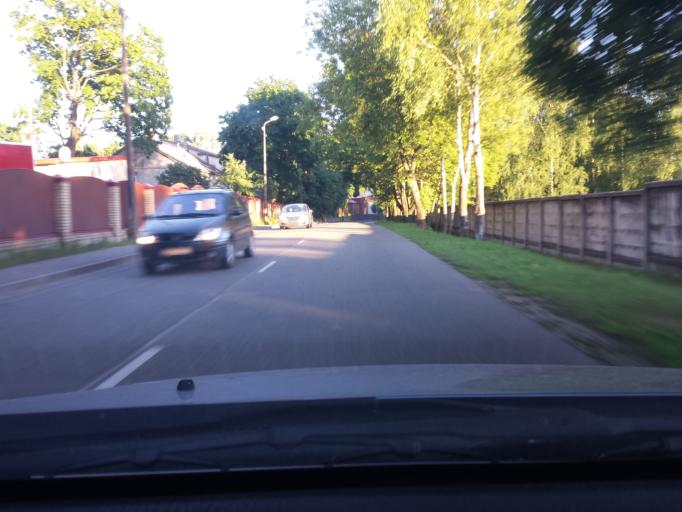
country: LV
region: Riga
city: Jaunciems
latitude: 57.0482
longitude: 24.1732
